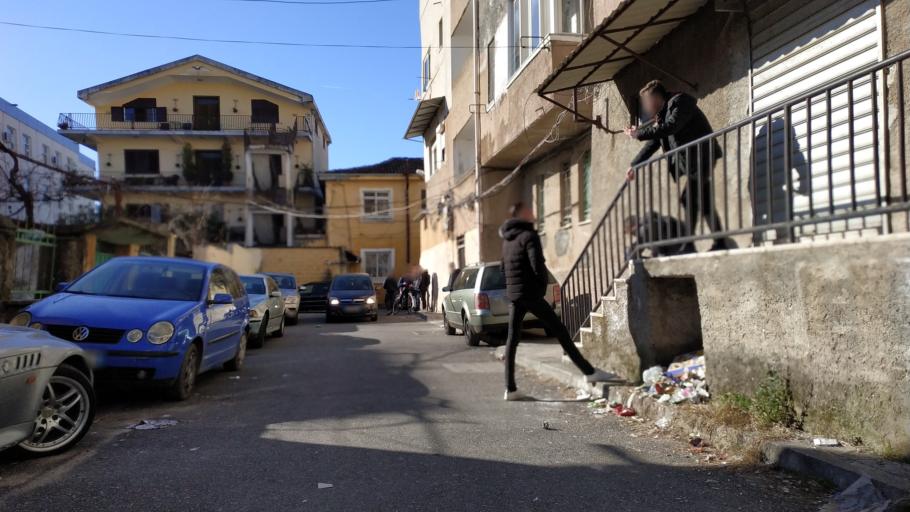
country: AL
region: Shkoder
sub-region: Rrethi i Shkodres
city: Shkoder
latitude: 42.0686
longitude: 19.5083
